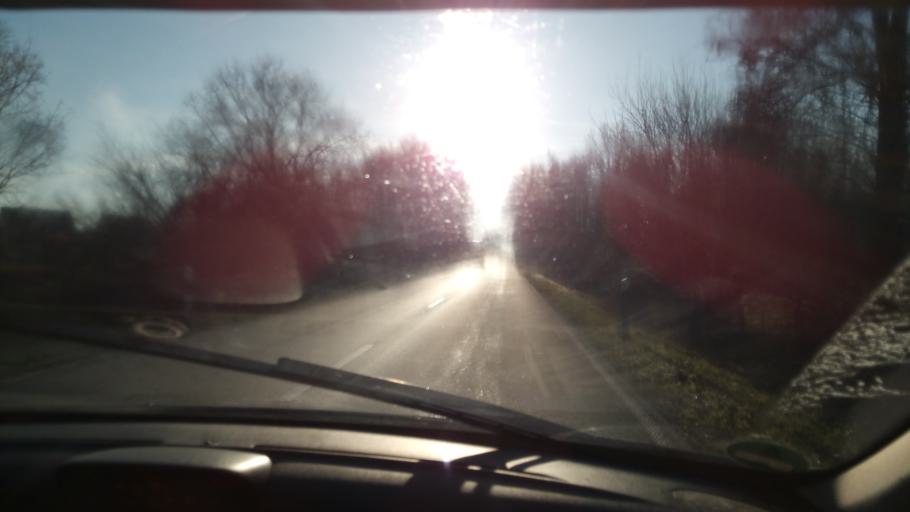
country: DE
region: Schleswig-Holstein
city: Witzeeze
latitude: 53.4500
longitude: 10.6119
